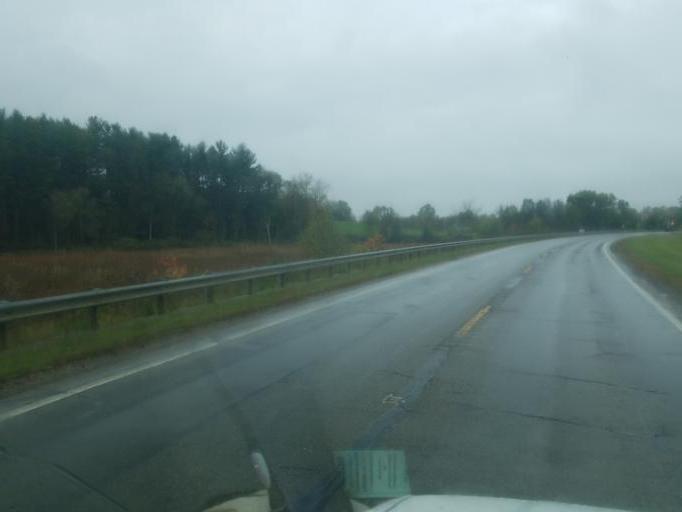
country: US
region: Ohio
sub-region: Holmes County
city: Millersburg
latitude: 40.6248
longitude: -81.9233
